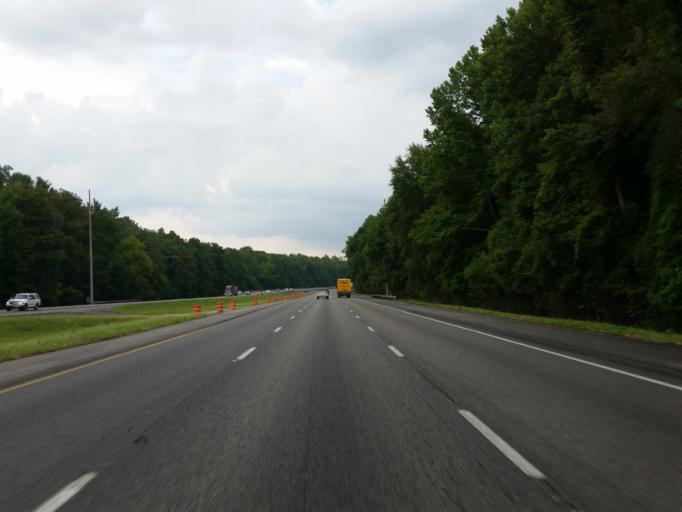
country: US
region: Georgia
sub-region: Bibb County
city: West Point
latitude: 32.7771
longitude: -83.7136
